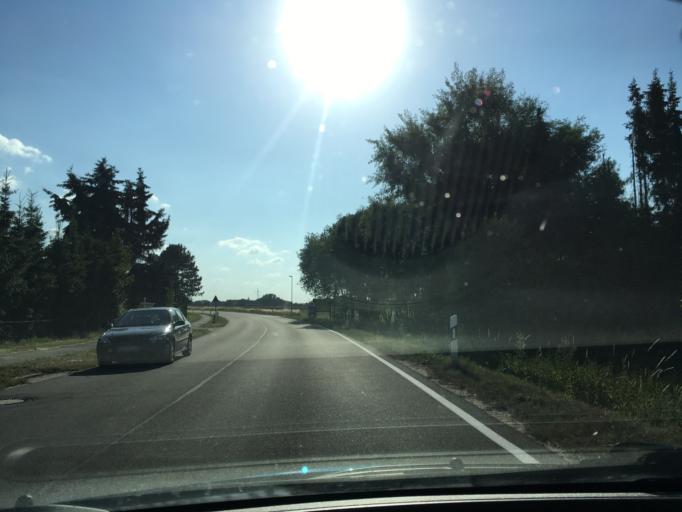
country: DE
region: Lower Saxony
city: Dahlenburg
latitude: 53.1844
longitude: 10.7305
